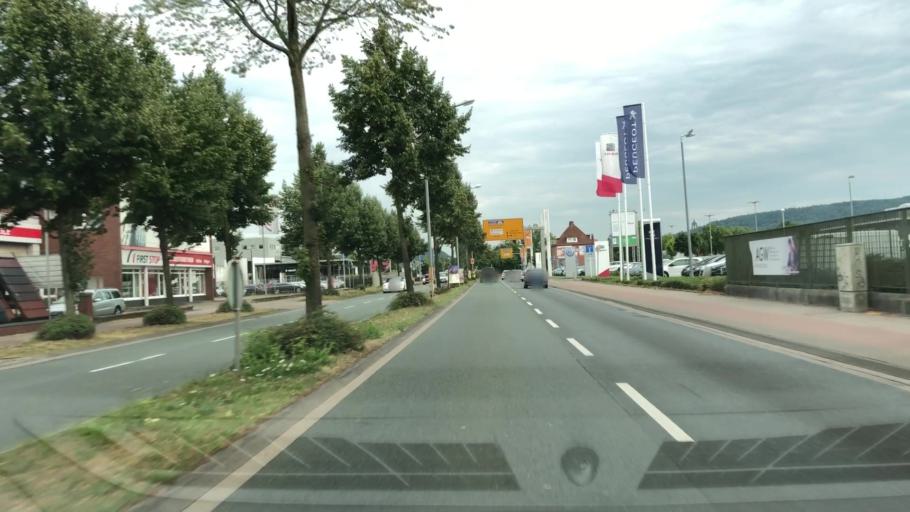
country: DE
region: North Rhine-Westphalia
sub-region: Regierungsbezirk Detmold
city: Minden
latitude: 52.2809
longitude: 8.9025
